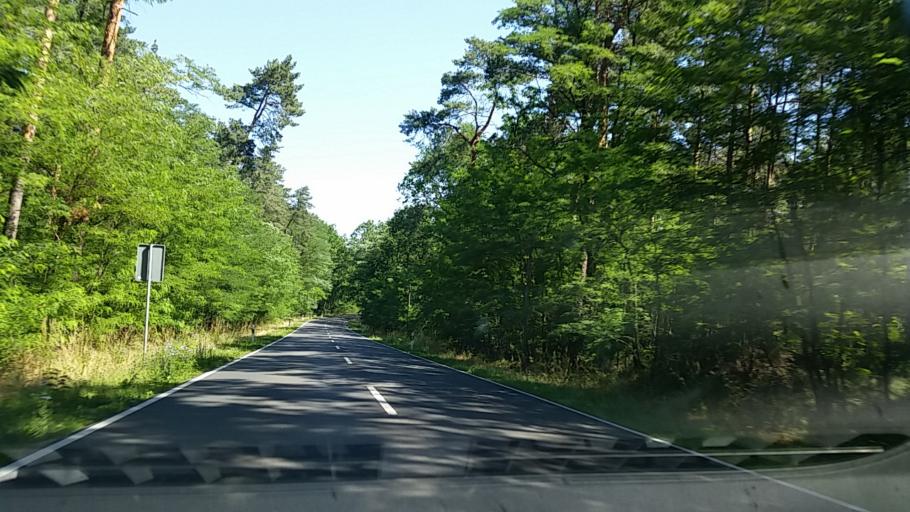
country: DE
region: Saxony-Anhalt
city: Kemberg
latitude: 51.7368
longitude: 12.6206
